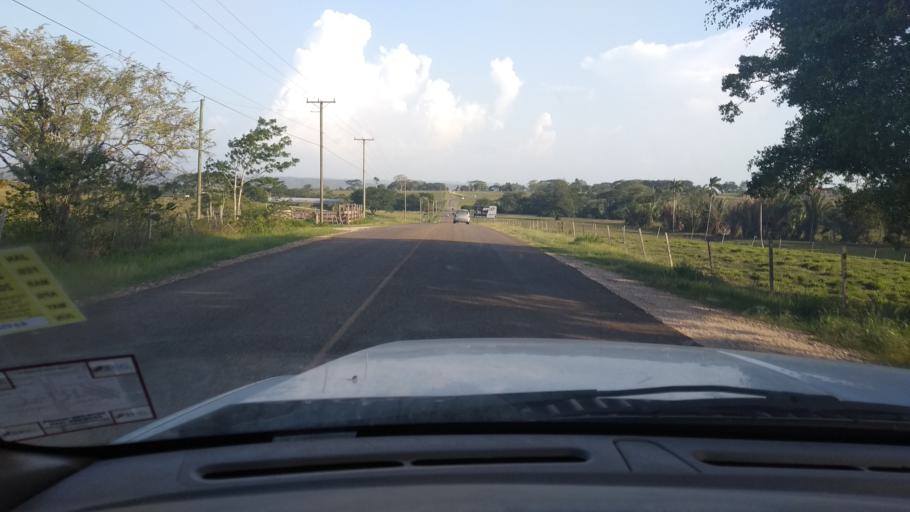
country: BZ
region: Cayo
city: San Ignacio
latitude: 17.2527
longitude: -88.9873
